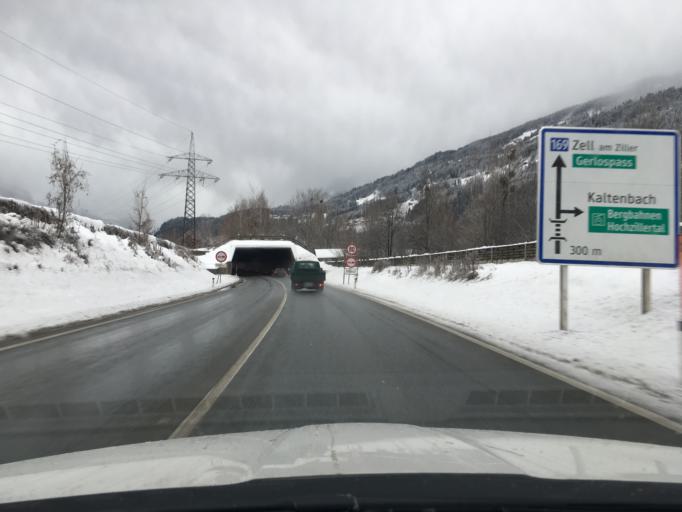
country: AT
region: Tyrol
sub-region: Politischer Bezirk Schwaz
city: Ried im Zillertal
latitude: 47.2949
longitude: 11.8763
